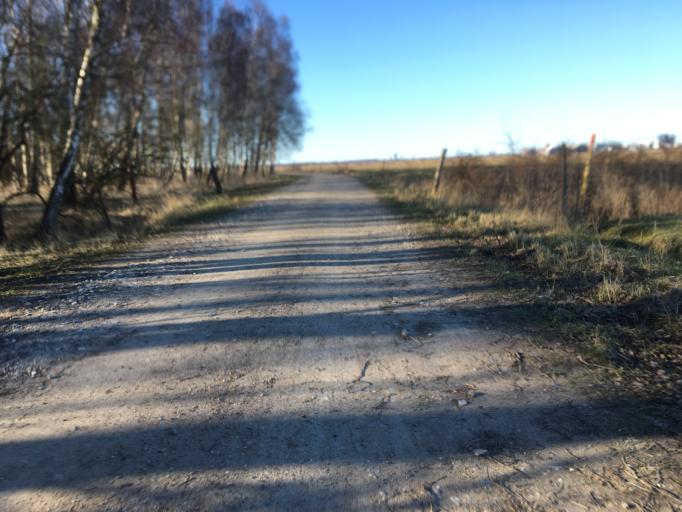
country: DK
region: Capital Region
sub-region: Tarnby Kommune
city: Tarnby
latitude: 55.5936
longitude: 12.5688
